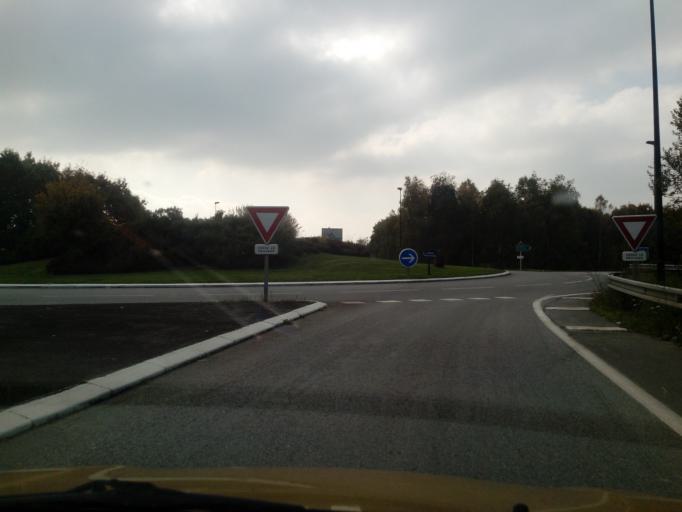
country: FR
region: Brittany
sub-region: Departement du Morbihan
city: Ploermel
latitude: 47.9193
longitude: -2.3871
